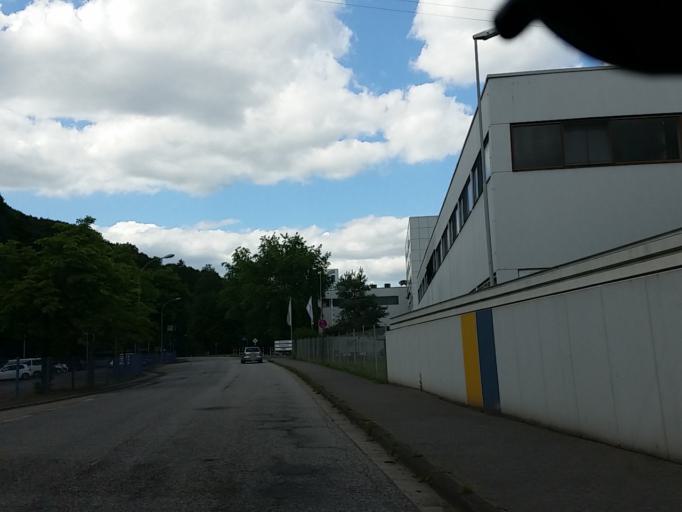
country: DE
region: Saarland
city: Wadern
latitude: 49.4981
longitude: 6.8671
